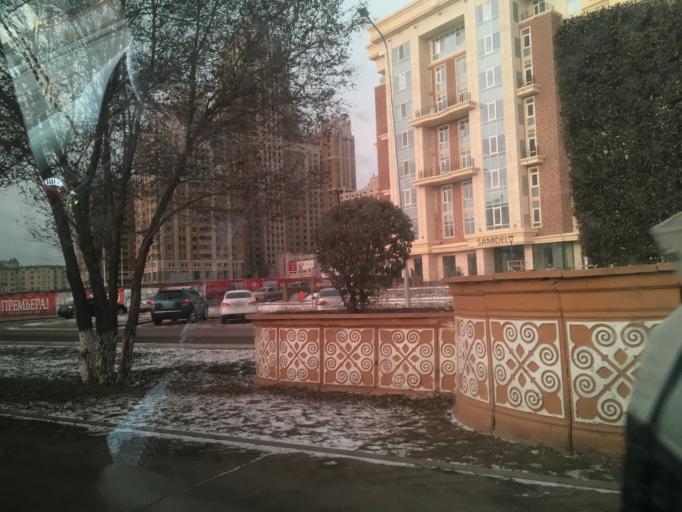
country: KZ
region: Astana Qalasy
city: Astana
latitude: 51.1411
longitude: 71.4186
